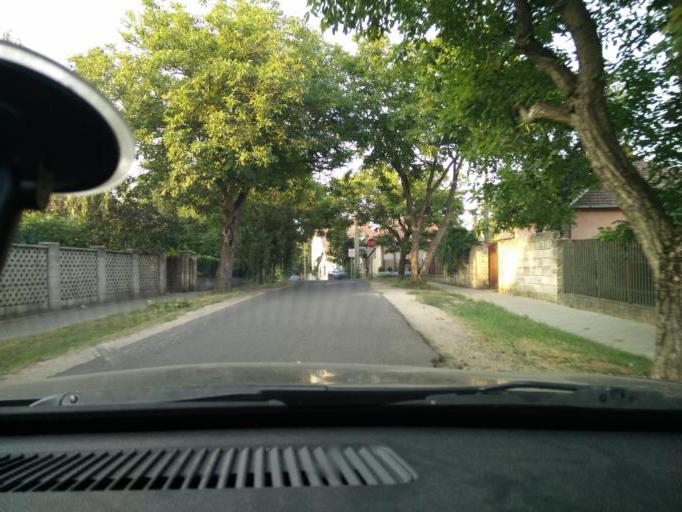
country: HU
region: Pest
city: Toeroekbalint
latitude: 47.4355
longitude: 18.9093
